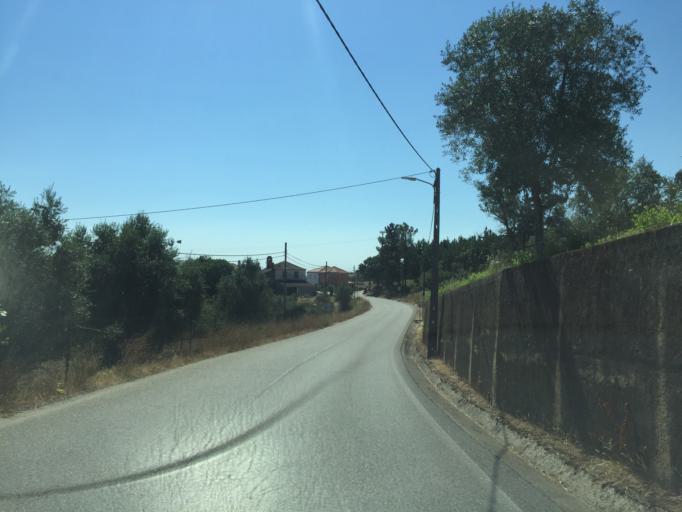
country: PT
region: Santarem
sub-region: Ferreira do Zezere
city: Ferreira do Zezere
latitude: 39.5979
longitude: -8.2985
